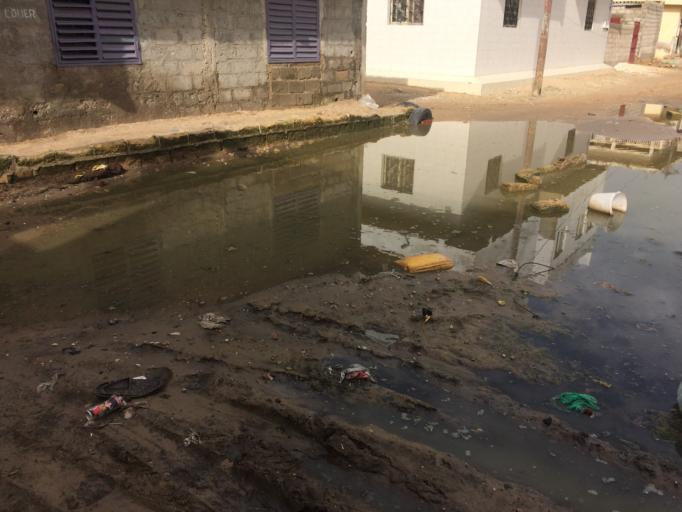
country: SN
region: Dakar
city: Pikine
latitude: 14.7451
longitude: -17.3221
